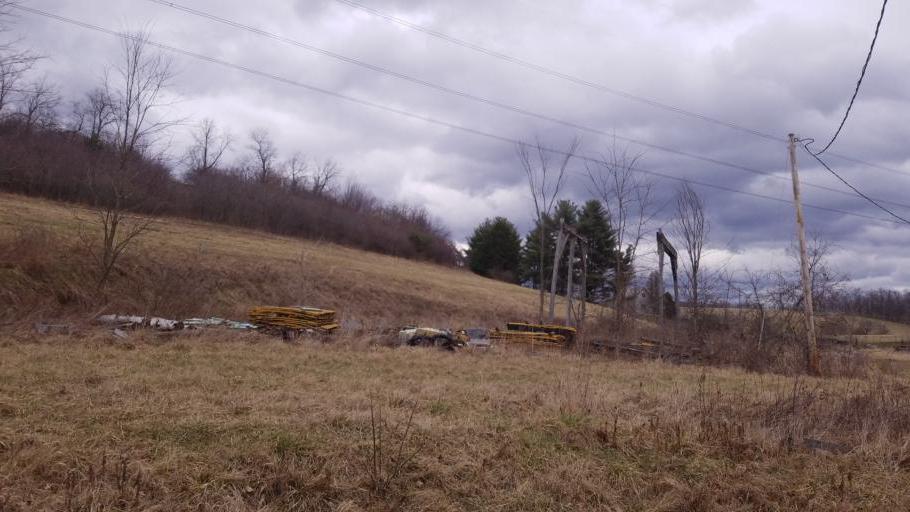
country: US
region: Ohio
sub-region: Muskingum County
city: Frazeysburg
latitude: 40.1361
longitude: -82.2279
